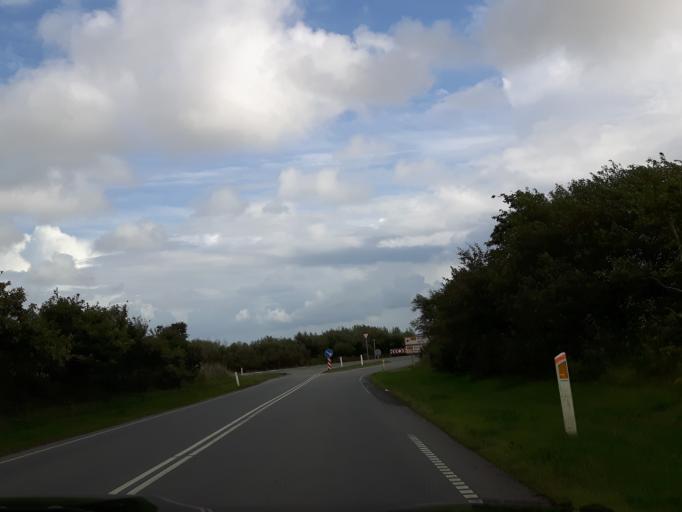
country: DK
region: North Denmark
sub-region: Thisted Kommune
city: Hurup
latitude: 56.7585
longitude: 8.4497
